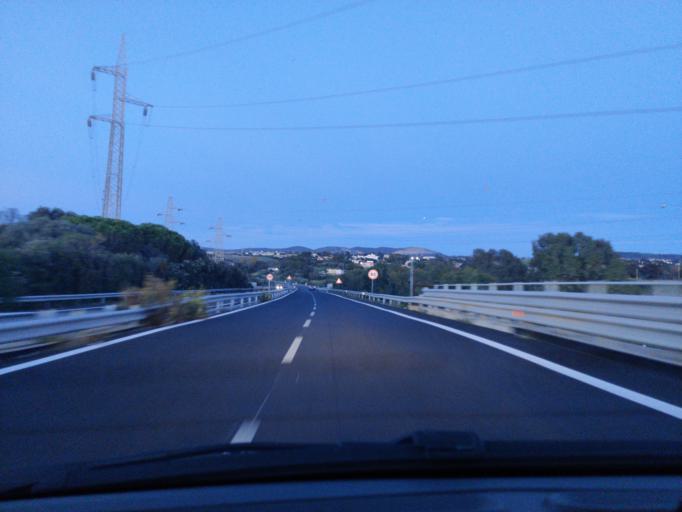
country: IT
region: Latium
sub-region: Citta metropolitana di Roma Capitale
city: Civitavecchia
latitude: 42.1051
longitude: 11.7882
